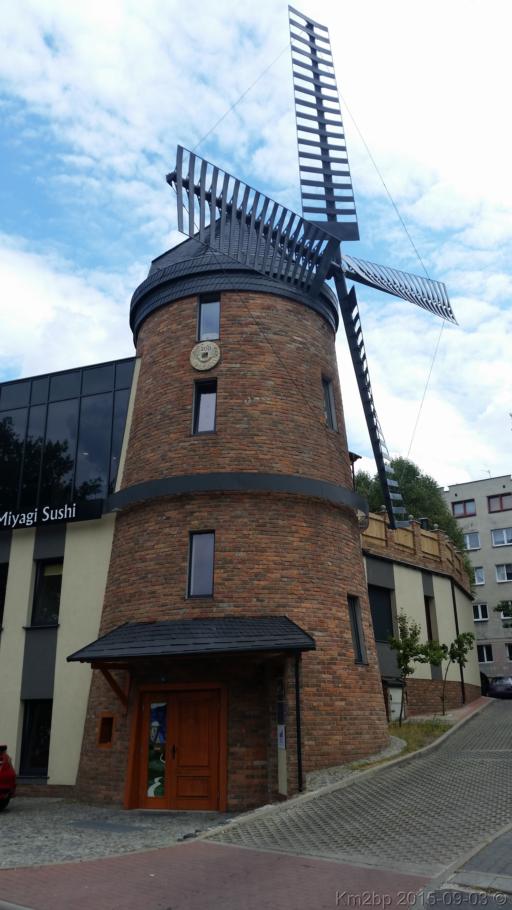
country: PL
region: Lubusz
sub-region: Zielona Gora
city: Zielona Gora
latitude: 51.9439
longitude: 15.5066
